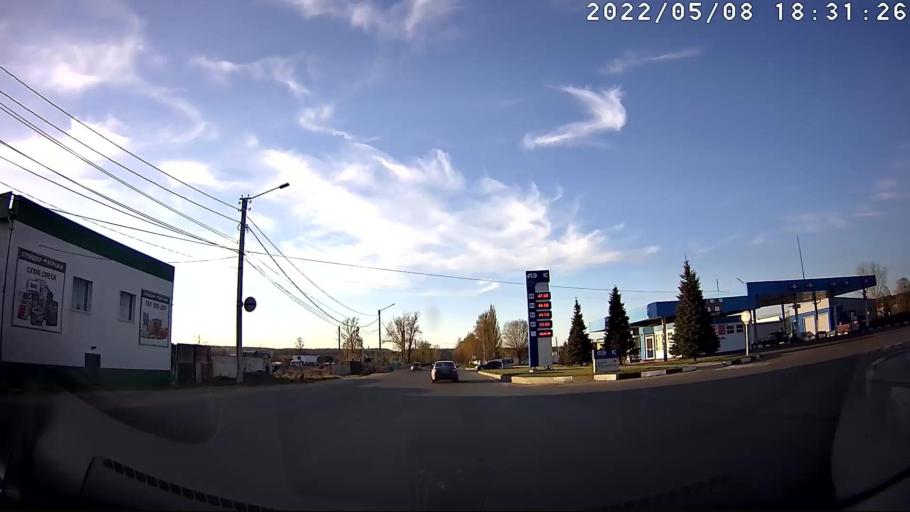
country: RU
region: Mariy-El
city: Volzhsk
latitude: 55.8797
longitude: 48.3598
